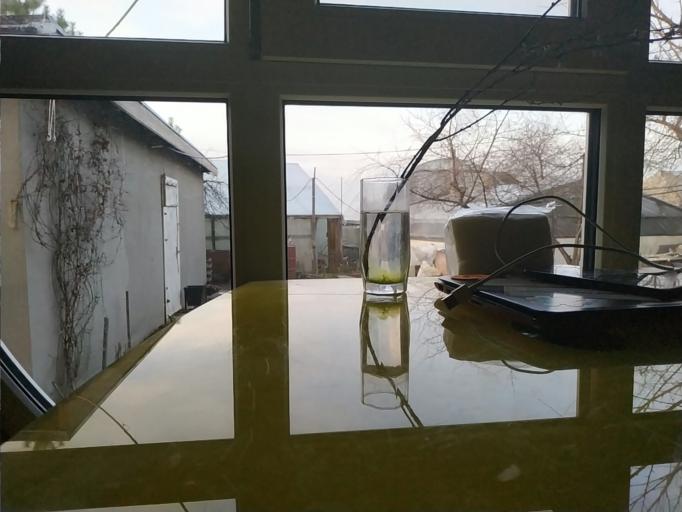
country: RU
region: Republic of Karelia
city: Suoyarvi
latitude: 62.3909
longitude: 32.0310
